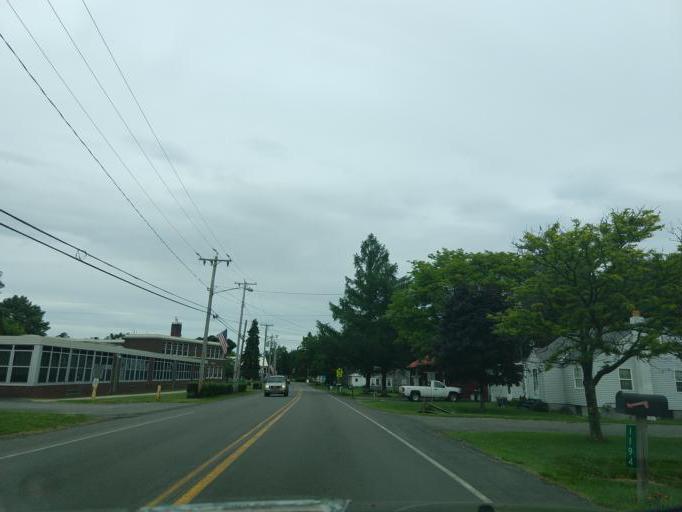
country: US
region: New York
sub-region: Cortland County
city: Munsons Corners
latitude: 42.5087
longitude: -76.1953
